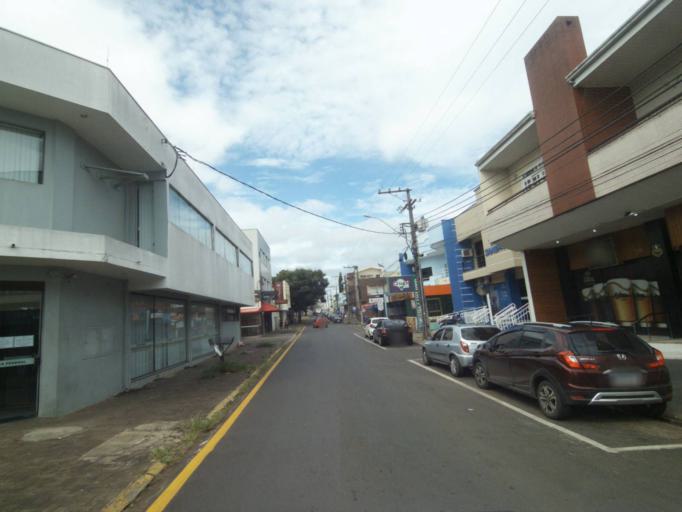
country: BR
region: Parana
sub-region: Telemaco Borba
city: Telemaco Borba
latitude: -24.3251
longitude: -50.6212
